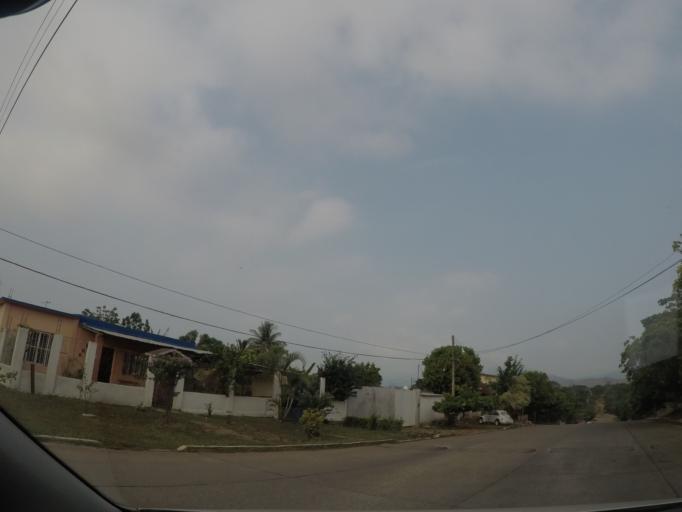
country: MX
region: Oaxaca
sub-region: Santa Maria Petapa
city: Llano Suchiapa
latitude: 16.8678
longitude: -95.0476
